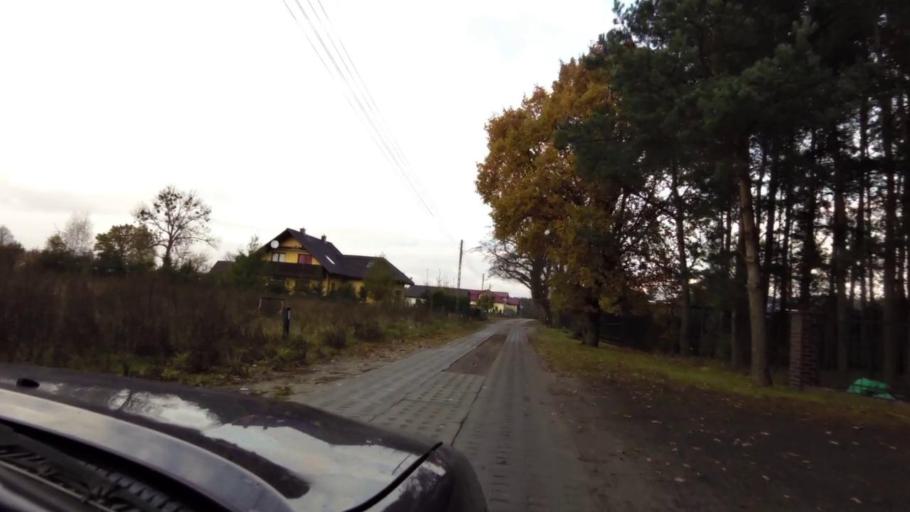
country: PL
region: West Pomeranian Voivodeship
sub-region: Powiat goleniowski
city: Goleniow
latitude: 53.5860
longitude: 14.7622
